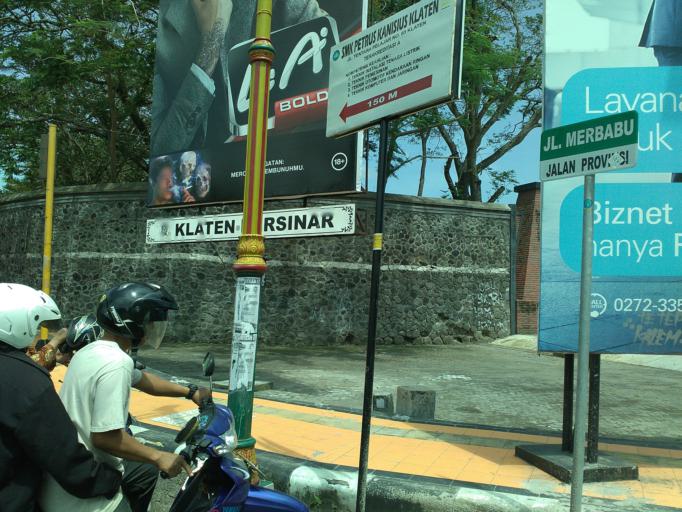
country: ID
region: Central Java
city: Klaten
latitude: -7.7066
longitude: 110.5971
